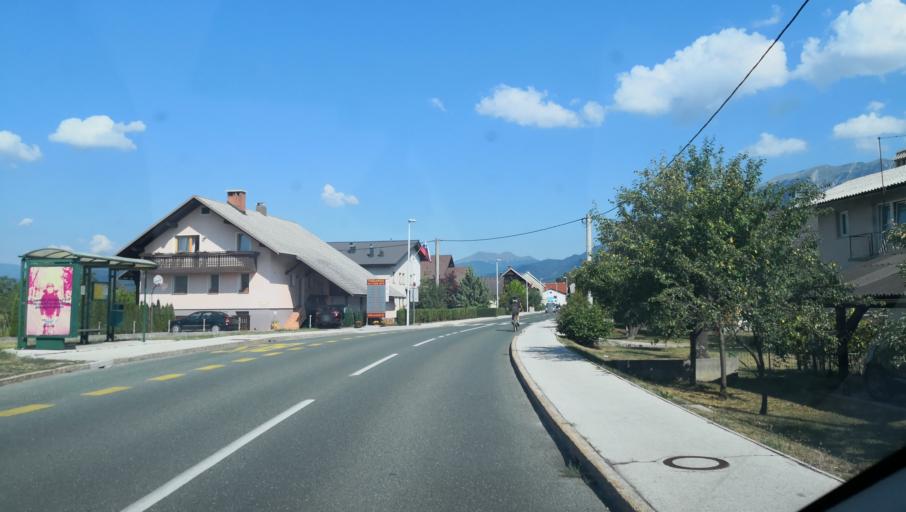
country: SI
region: Radovljica
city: Lesce
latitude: 46.3578
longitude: 14.1629
